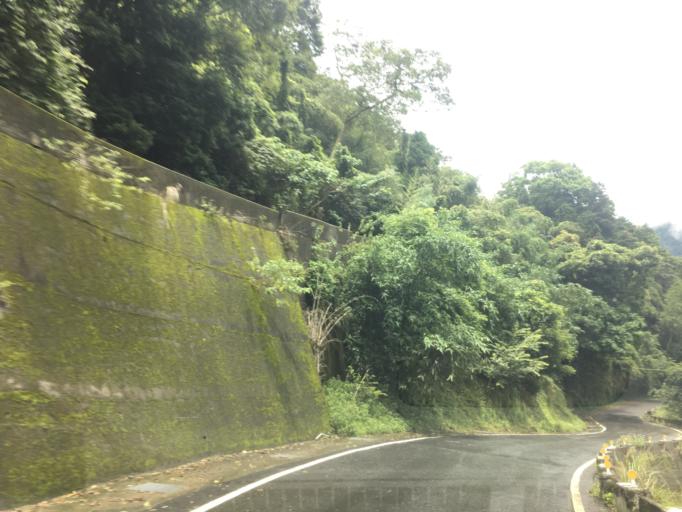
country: TW
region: Taiwan
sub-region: Yunlin
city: Douliu
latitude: 23.5516
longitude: 120.6788
